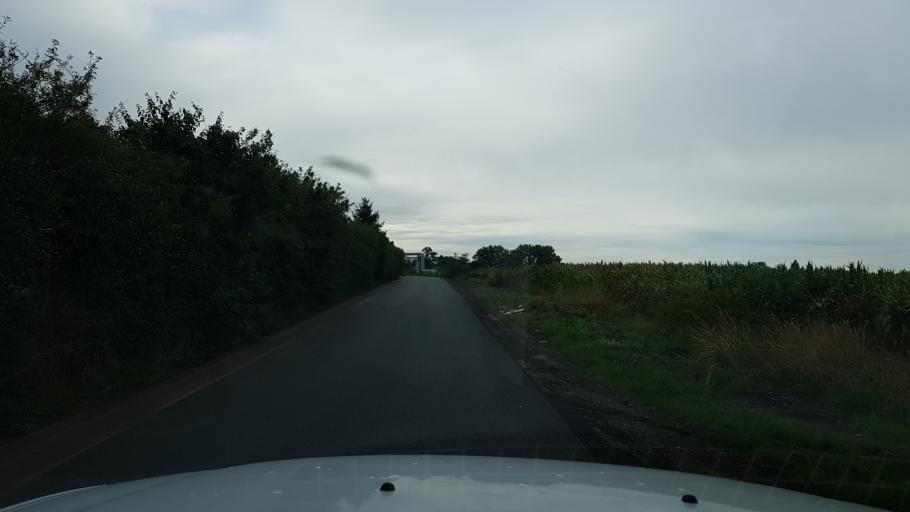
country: PL
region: West Pomeranian Voivodeship
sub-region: Powiat stargardzki
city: Stargard Szczecinski
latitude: 53.3225
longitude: 15.0268
